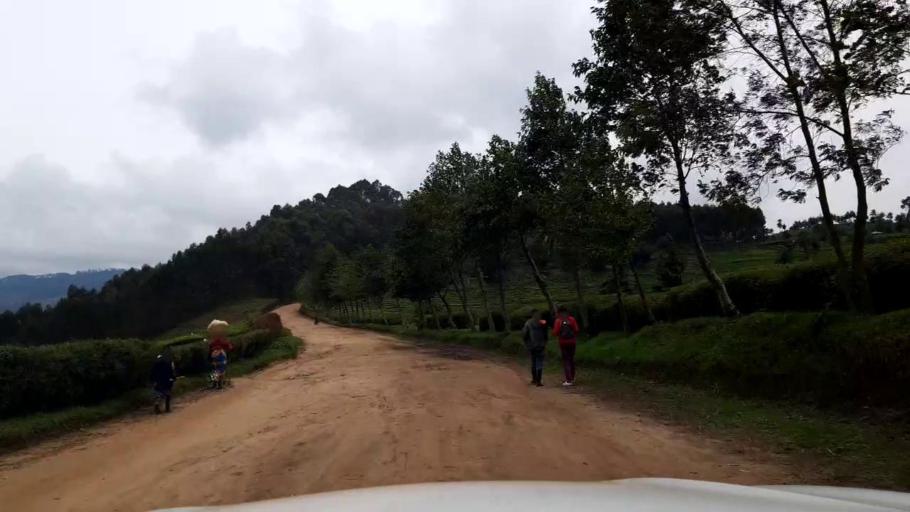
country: RW
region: Western Province
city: Kibuye
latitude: -1.9529
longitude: 29.4076
